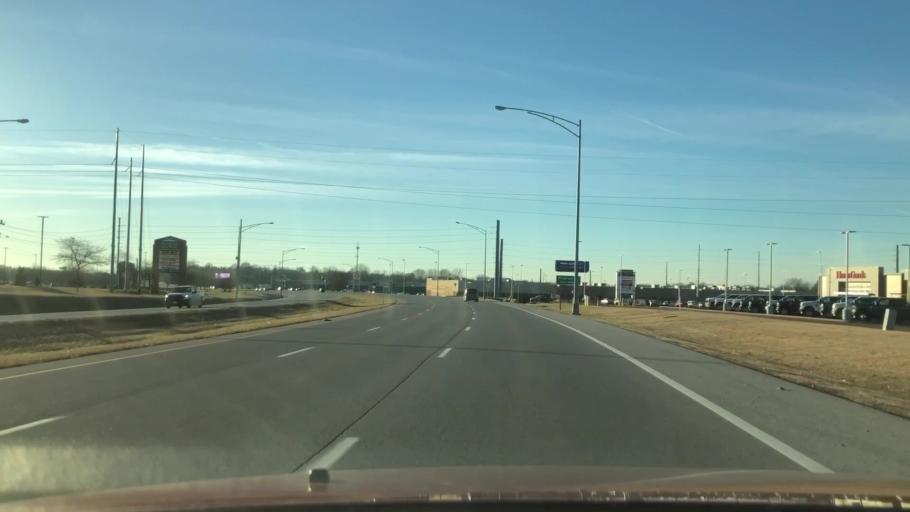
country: US
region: Missouri
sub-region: Greene County
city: Springfield
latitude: 37.1549
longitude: -93.2629
